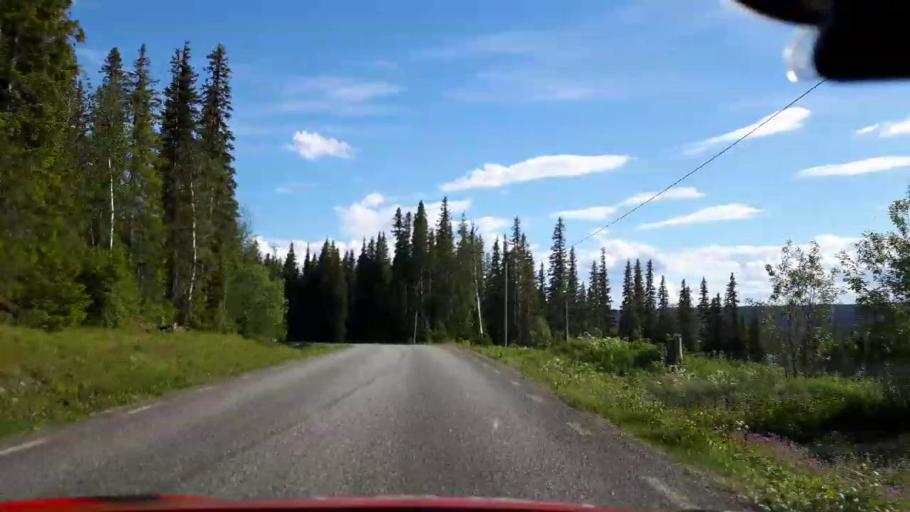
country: SE
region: Jaemtland
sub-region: Krokoms Kommun
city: Valla
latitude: 63.7125
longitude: 14.1369
